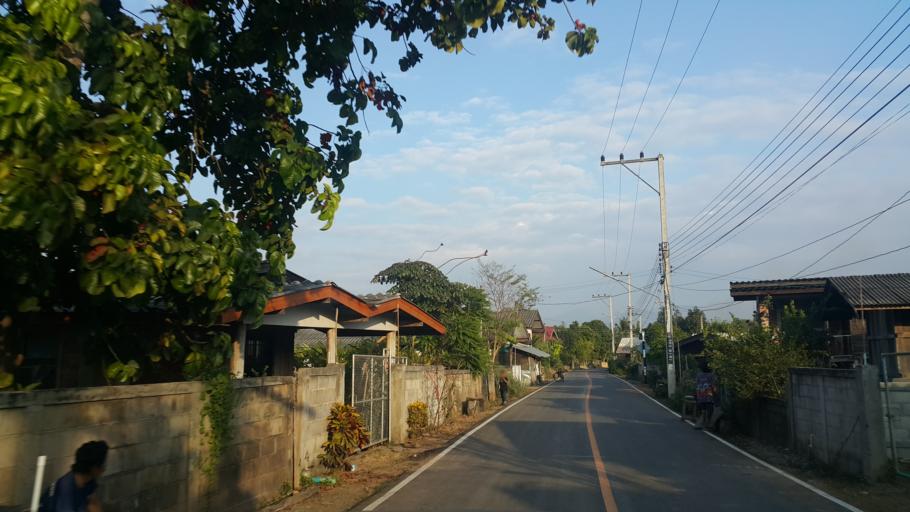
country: TH
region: Lampang
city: Sop Prap
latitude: 17.9433
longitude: 99.3411
